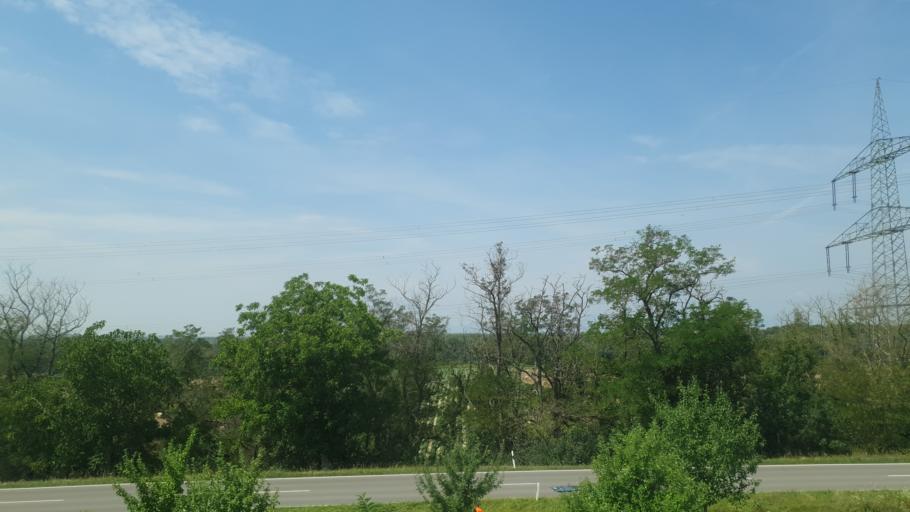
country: DE
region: Baden-Wuerttemberg
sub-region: Freiburg Region
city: Schliengen
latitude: 47.7501
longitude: 7.5620
